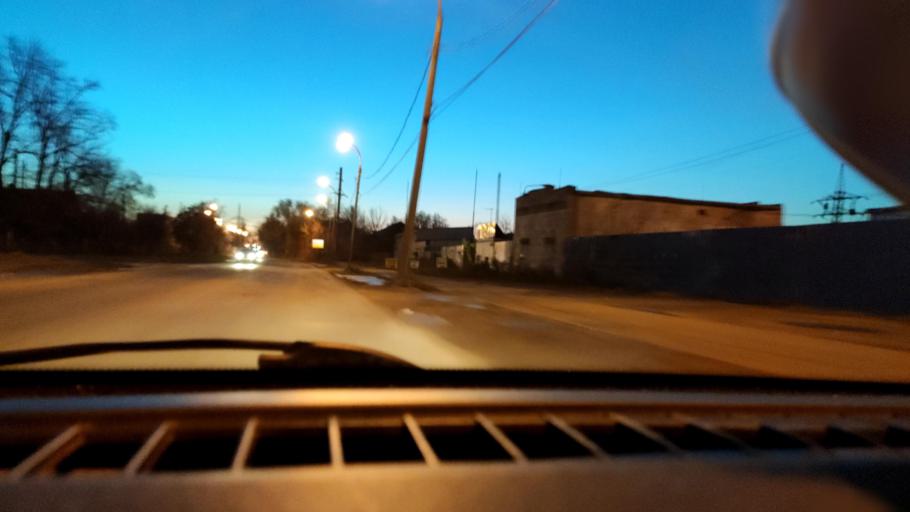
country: RU
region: Samara
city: Samara
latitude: 53.1341
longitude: 50.1183
